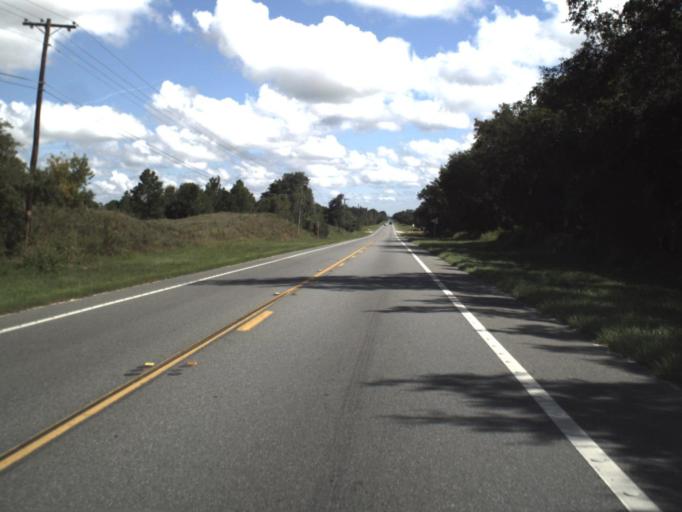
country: US
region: Florida
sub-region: Polk County
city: Davenport
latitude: 28.1939
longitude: -81.5855
